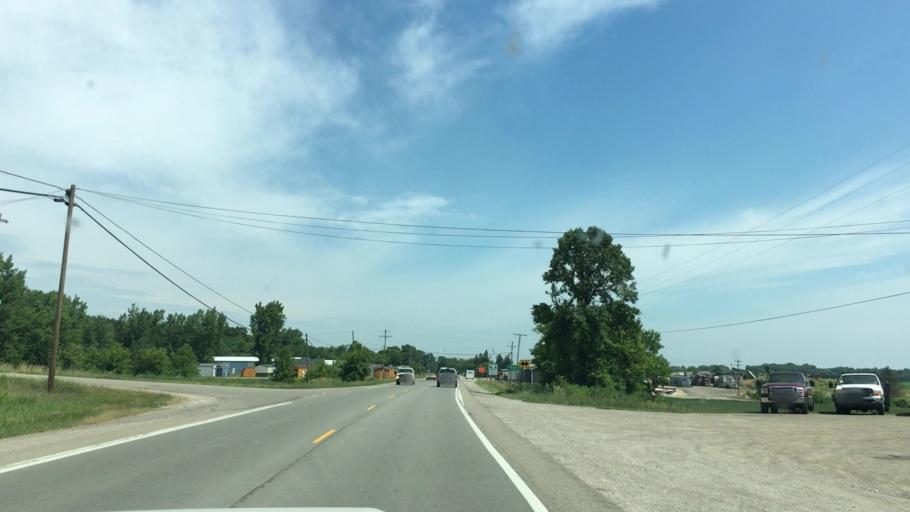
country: US
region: Michigan
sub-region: Lapeer County
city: Imlay City
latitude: 43.0489
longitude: -83.0723
